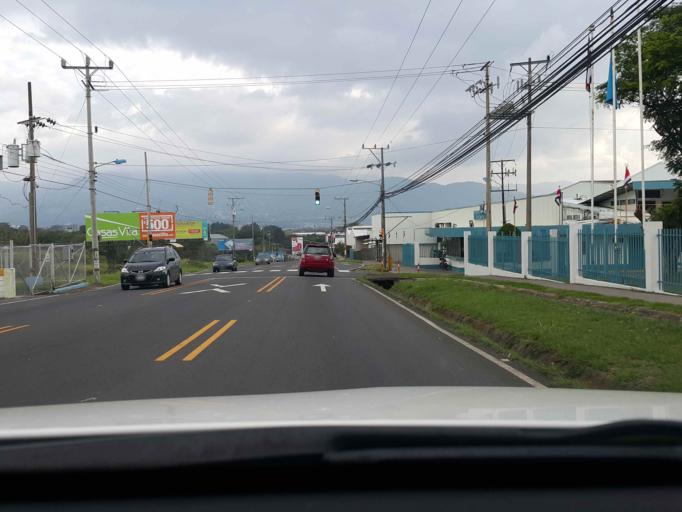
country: CR
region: Heredia
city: San Francisco
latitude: 9.9753
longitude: -84.1122
